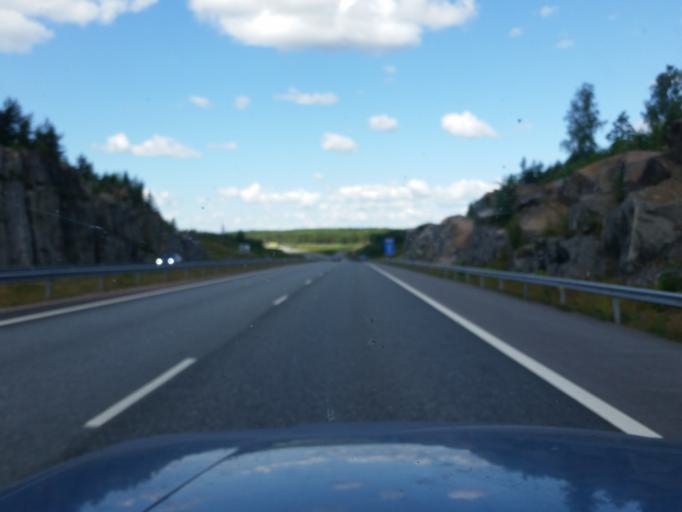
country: FI
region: Varsinais-Suomi
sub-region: Salo
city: Suomusjaervi
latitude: 60.3762
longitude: 23.6378
